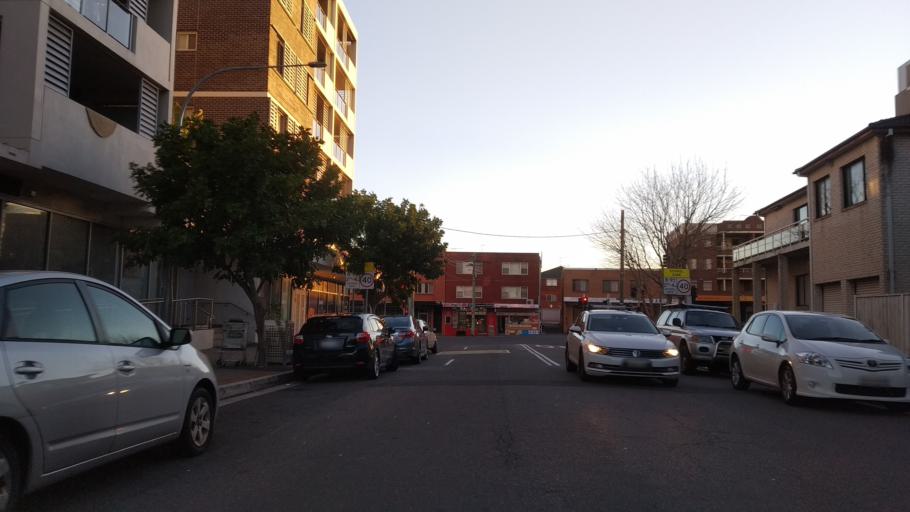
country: AU
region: New South Wales
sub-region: Randwick
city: Maroubra
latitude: -33.9574
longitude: 151.2315
